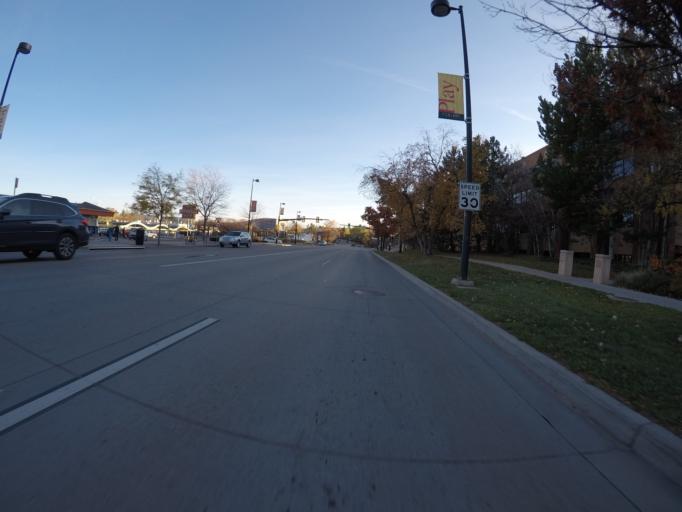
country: US
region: Colorado
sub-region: Boulder County
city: Boulder
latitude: 40.0262
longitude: -105.2821
